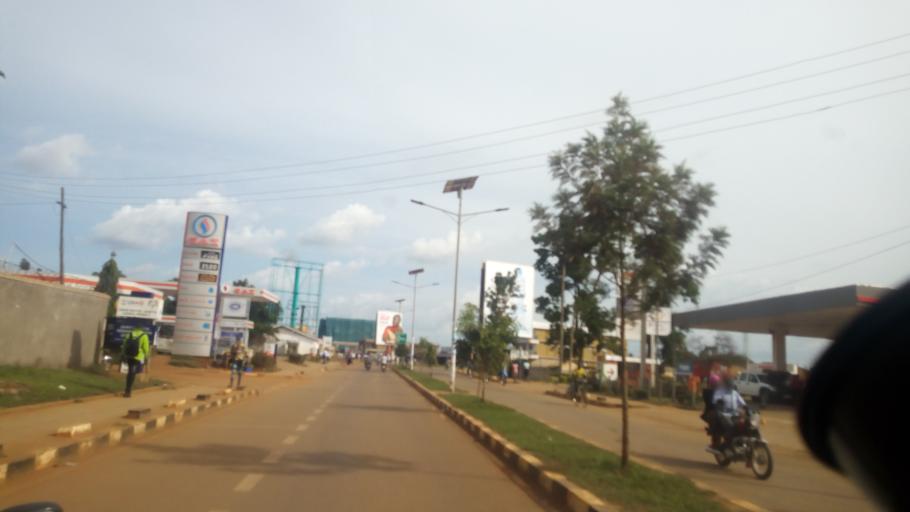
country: UG
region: Northern Region
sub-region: Lira District
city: Lira
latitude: 2.2349
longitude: 32.8932
